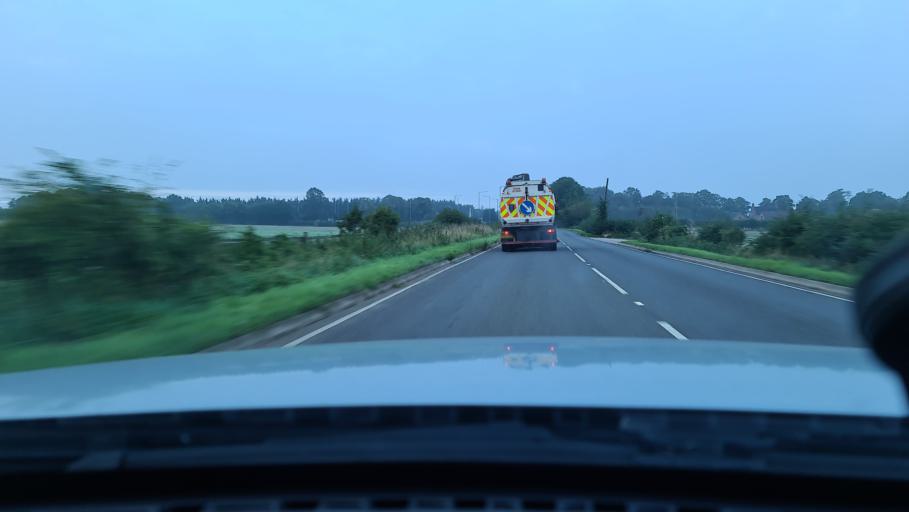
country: GB
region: England
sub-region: Warwickshire
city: Wolston
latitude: 52.3589
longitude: -1.3914
